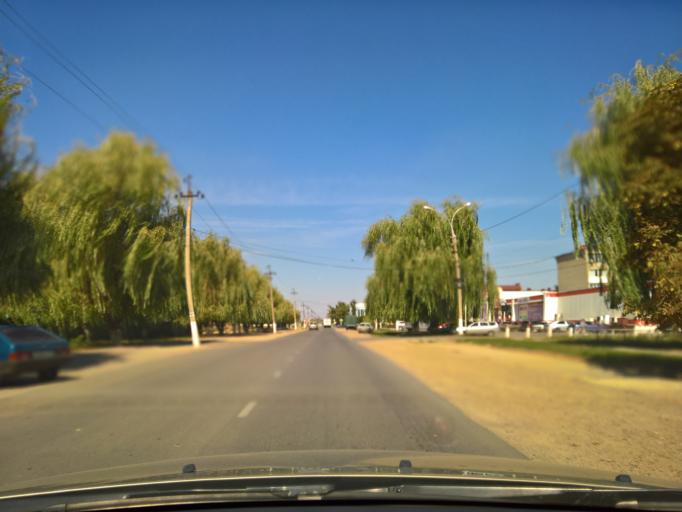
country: RU
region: Krasnodarskiy
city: Slavyansk-na-Kubani
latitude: 45.2652
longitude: 38.1047
